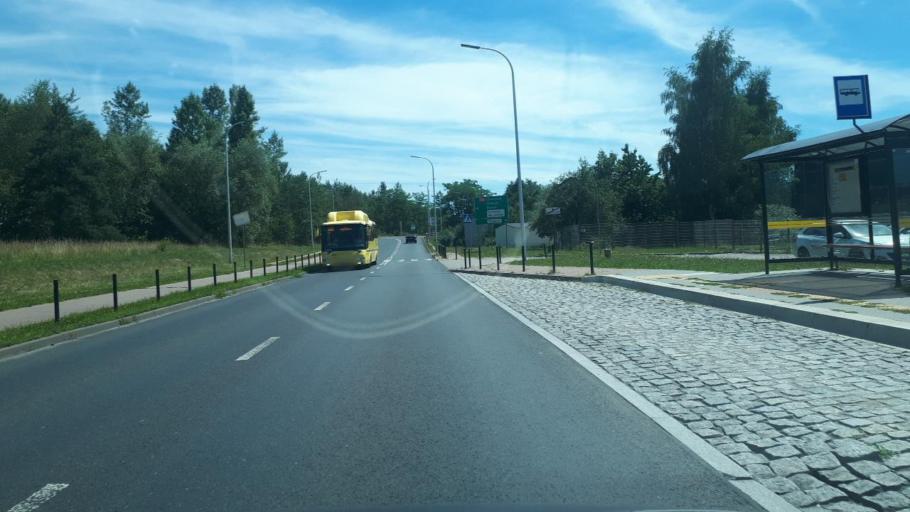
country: PL
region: Silesian Voivodeship
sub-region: Tychy
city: Cielmice
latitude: 50.1019
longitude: 19.0435
